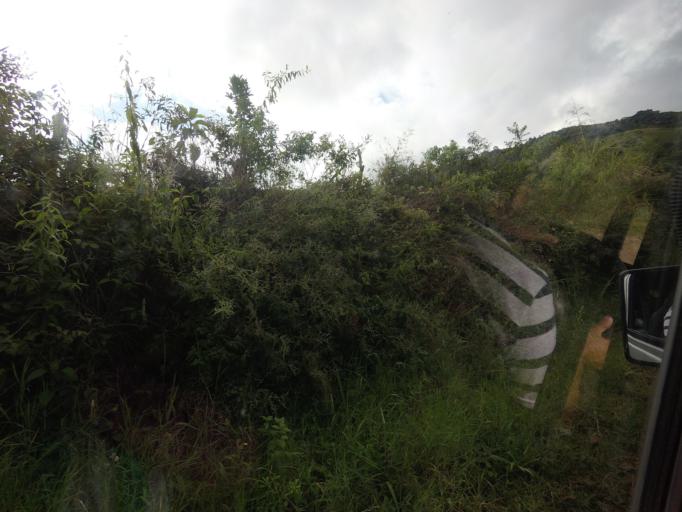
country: CO
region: Huila
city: San Agustin
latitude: 1.9233
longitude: -76.2937
